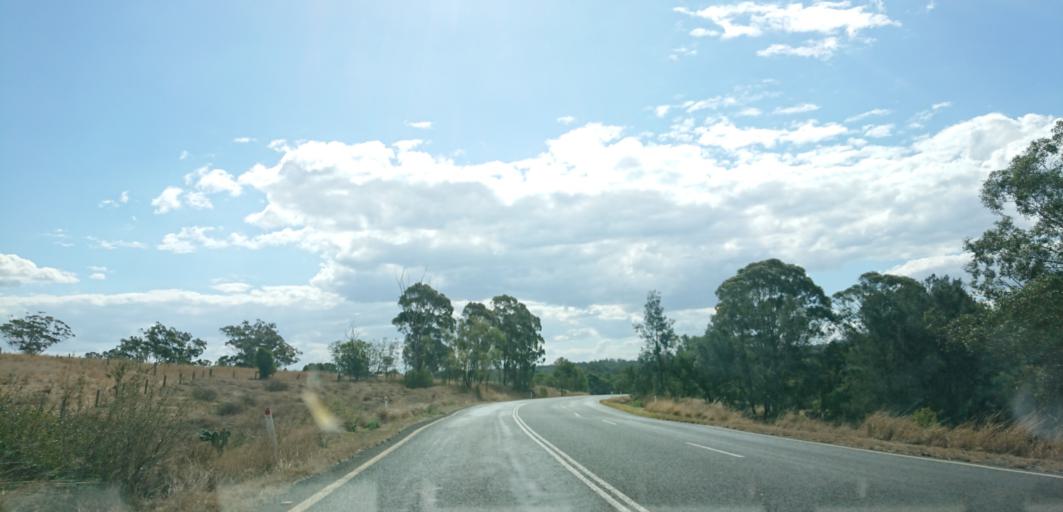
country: AU
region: Queensland
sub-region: Toowoomba
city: Top Camp
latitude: -27.7871
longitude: 152.0991
